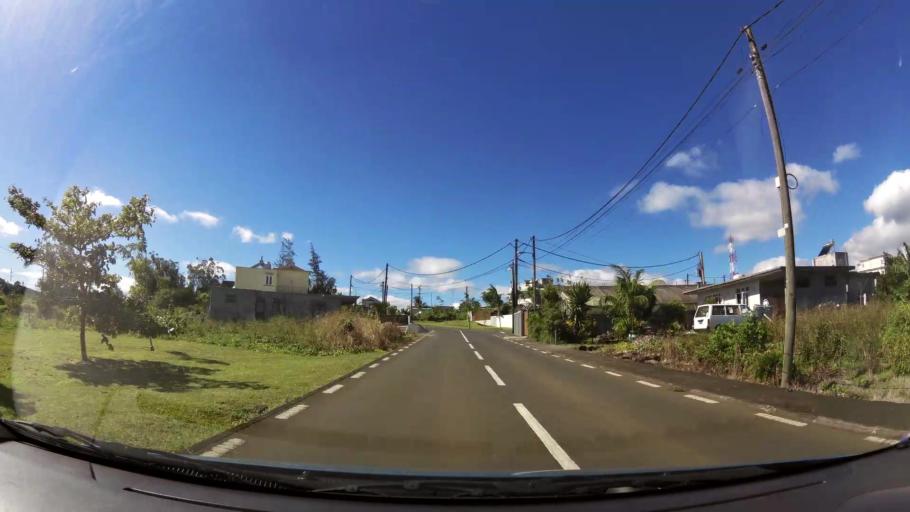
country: MU
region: Plaines Wilhems
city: Curepipe
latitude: -20.3418
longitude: 57.4917
